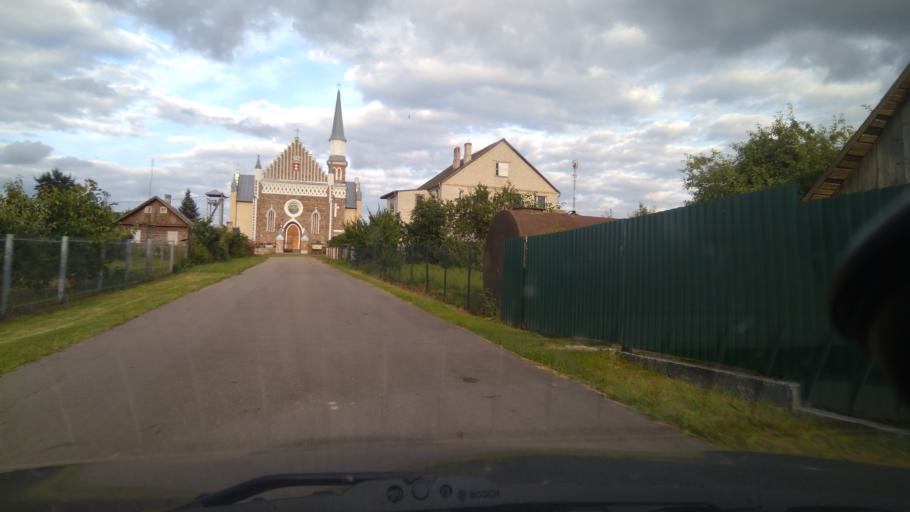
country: BY
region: Grodnenskaya
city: Shchuchin
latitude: 53.5374
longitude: 24.7303
